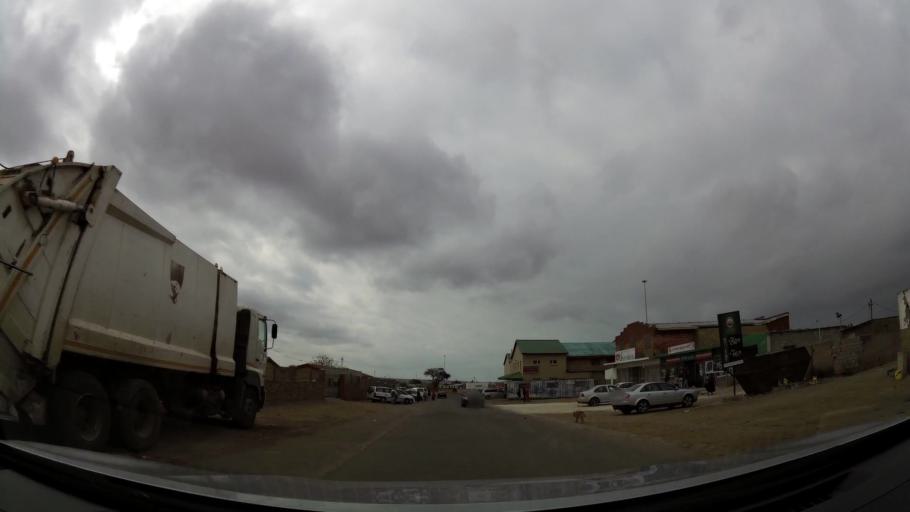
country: ZA
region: Eastern Cape
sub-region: Nelson Mandela Bay Metropolitan Municipality
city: Port Elizabeth
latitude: -33.8776
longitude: 25.5632
